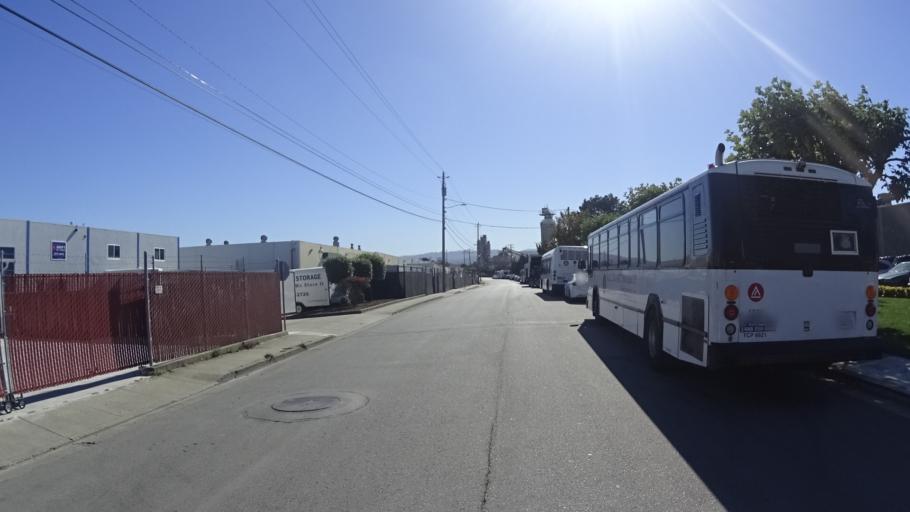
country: US
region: California
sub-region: San Mateo County
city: South San Francisco
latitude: 37.6452
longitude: -122.4112
